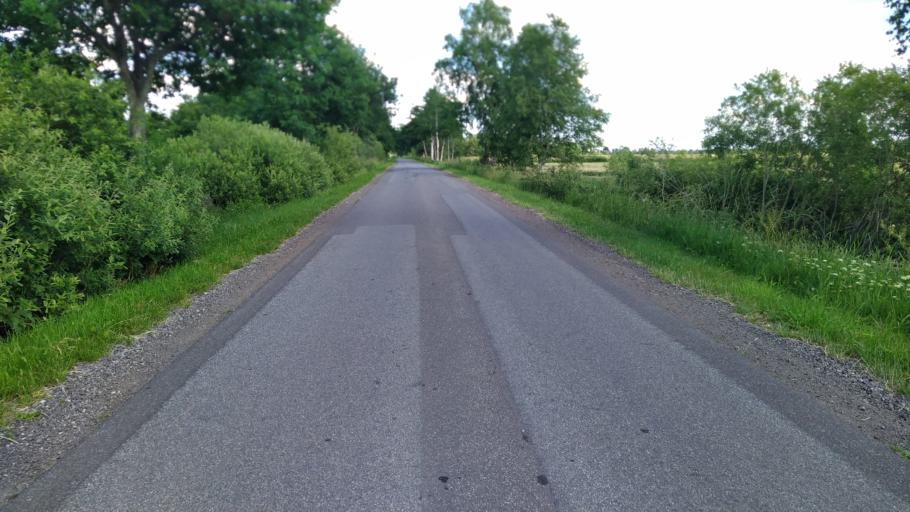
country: DE
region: Lower Saxony
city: Steinau
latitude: 53.6548
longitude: 8.9039
